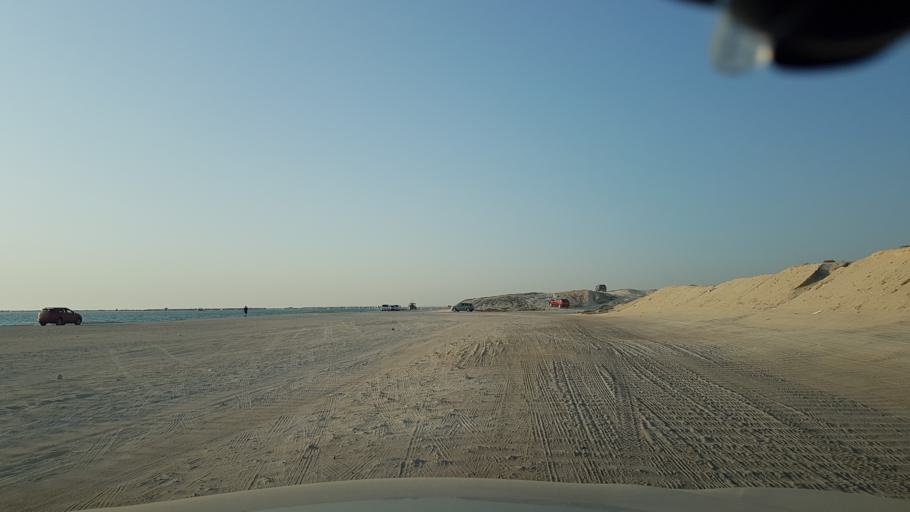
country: BH
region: Manama
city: Jidd Hafs
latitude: 26.2446
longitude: 50.5030
